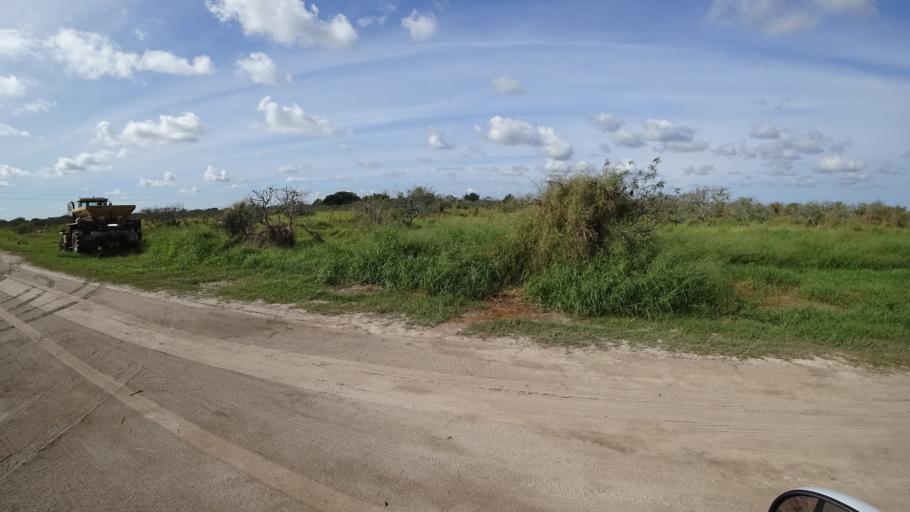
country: US
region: Florida
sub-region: Hillsborough County
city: Wimauma
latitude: 27.6057
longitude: -82.2880
